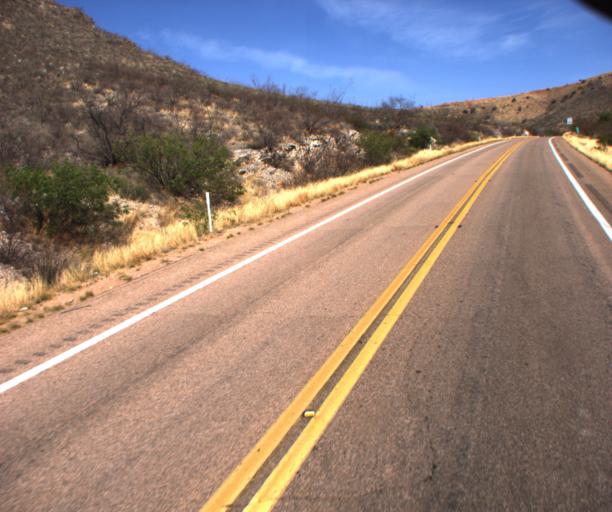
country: US
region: Arizona
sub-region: Cochise County
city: Bisbee
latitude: 31.5173
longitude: -110.0242
